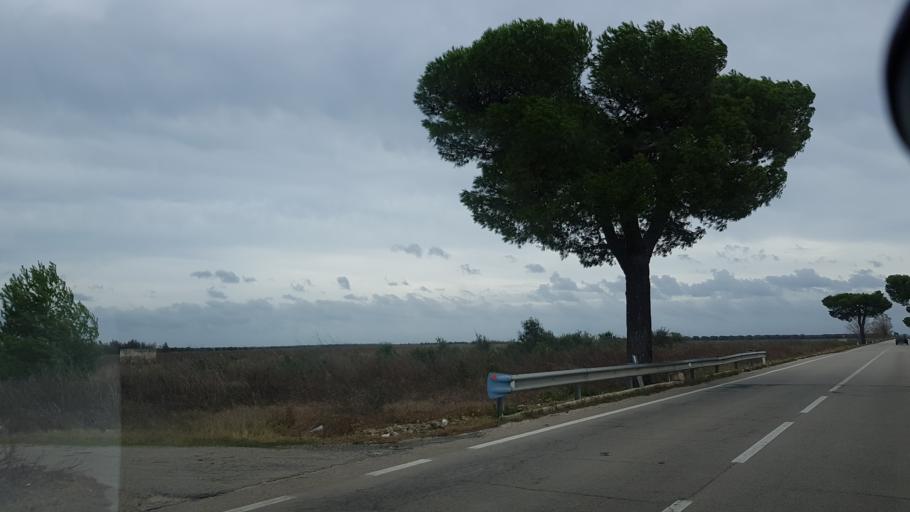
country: IT
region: Apulia
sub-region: Provincia di Brindisi
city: San Pancrazio Salentino
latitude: 40.4118
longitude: 17.8659
